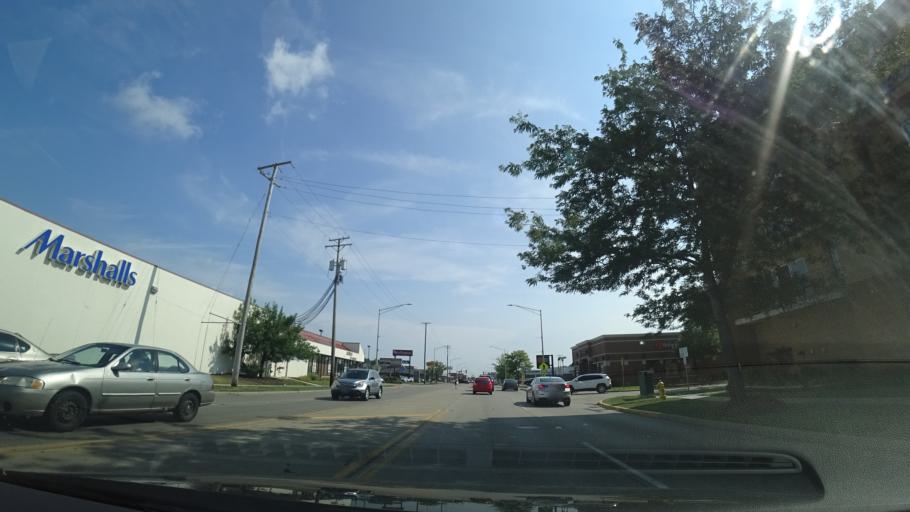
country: US
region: Illinois
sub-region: Cook County
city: Harwood Heights
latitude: 41.9659
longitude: -87.8073
